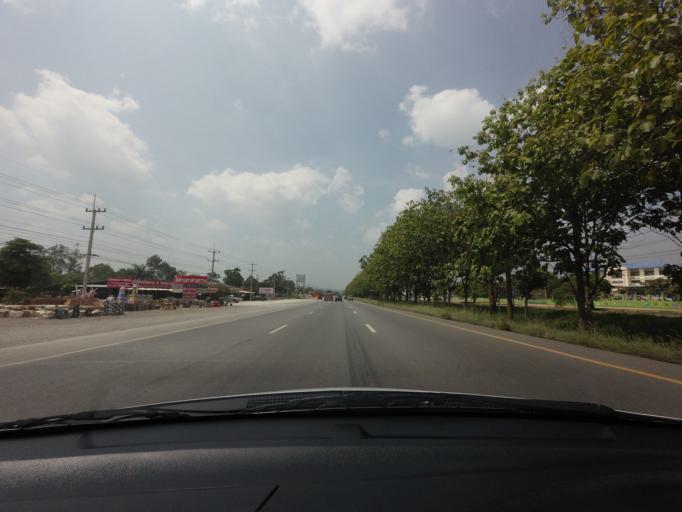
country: TH
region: Nakhon Ratchasima
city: Pak Chong
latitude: 14.6654
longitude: 101.4251
